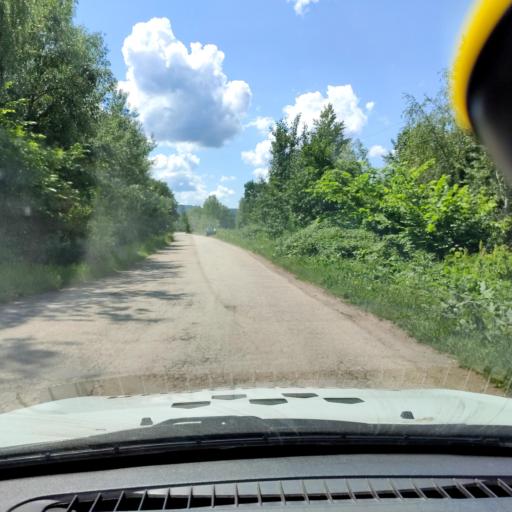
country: RU
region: Samara
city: Povolzhskiy
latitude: 53.4677
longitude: 49.6693
